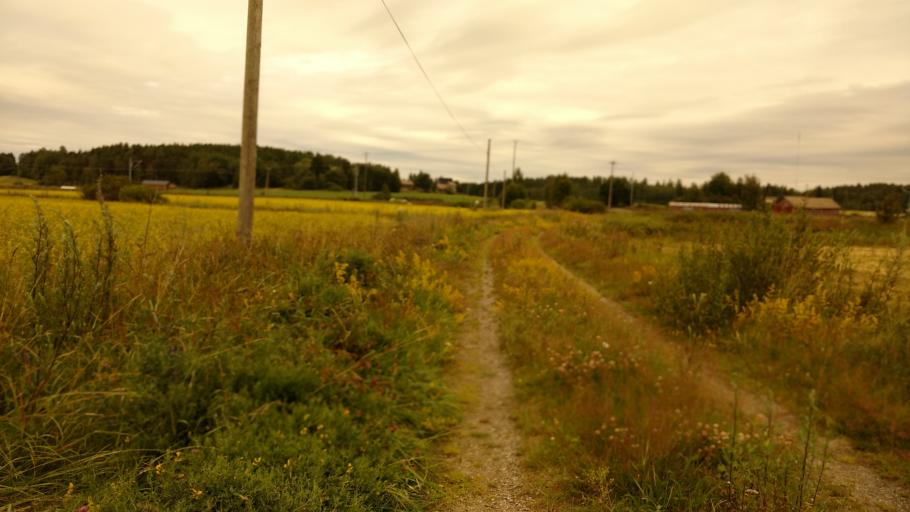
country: FI
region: Varsinais-Suomi
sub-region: Turku
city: Paimio
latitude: 60.4153
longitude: 22.8515
